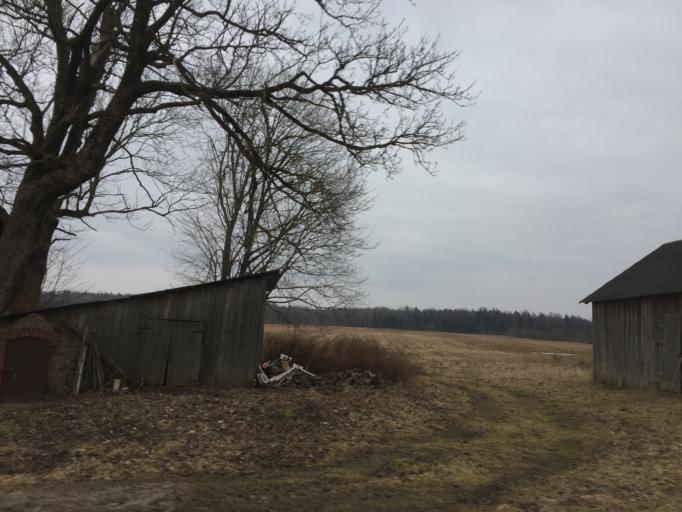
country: LV
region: Lielvarde
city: Lielvarde
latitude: 56.7573
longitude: 24.8424
